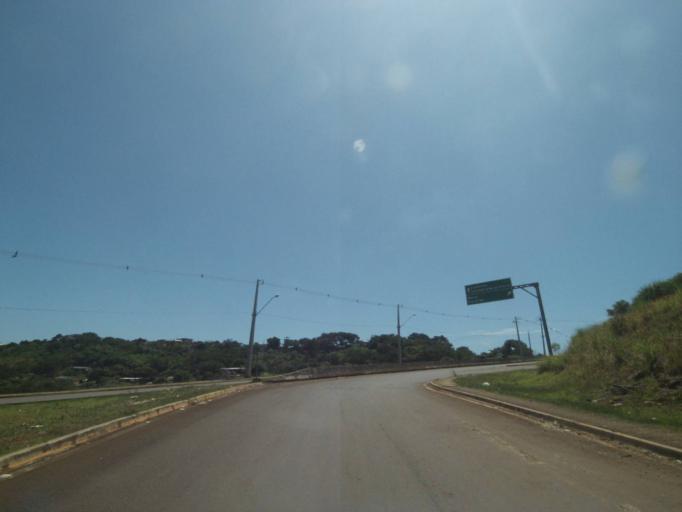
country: BR
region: Parana
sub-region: Londrina
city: Londrina
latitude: -23.3893
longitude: -51.1356
